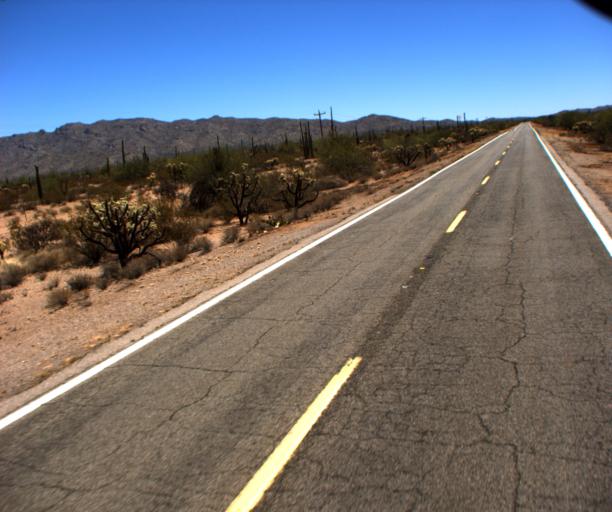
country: US
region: Arizona
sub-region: Pima County
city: Sells
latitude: 32.1825
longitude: -112.2917
